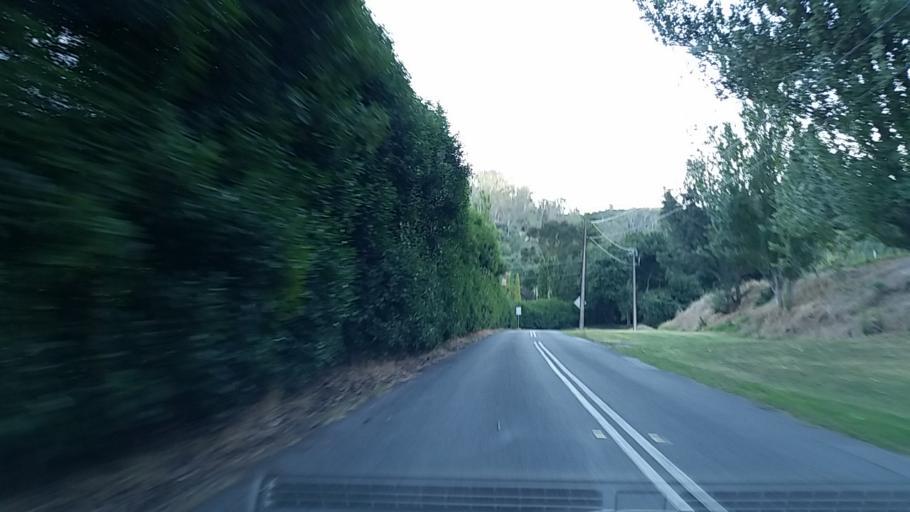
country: AU
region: South Australia
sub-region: Adelaide Hills
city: Adelaide Hills
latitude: -34.8834
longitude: 138.7529
